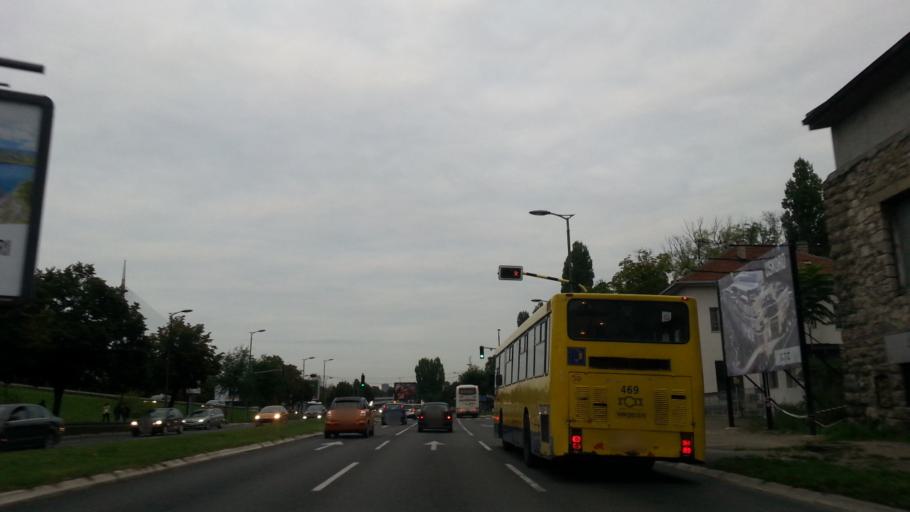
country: RS
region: Central Serbia
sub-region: Belgrade
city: Cukarica
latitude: 44.7878
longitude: 20.4177
